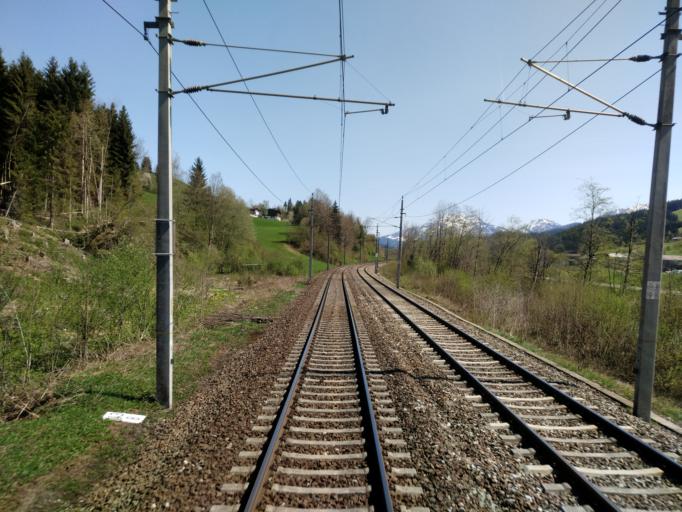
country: AT
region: Tyrol
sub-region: Politischer Bezirk Kitzbuhel
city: Sankt Johann in Tirol
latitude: 47.5058
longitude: 12.4760
